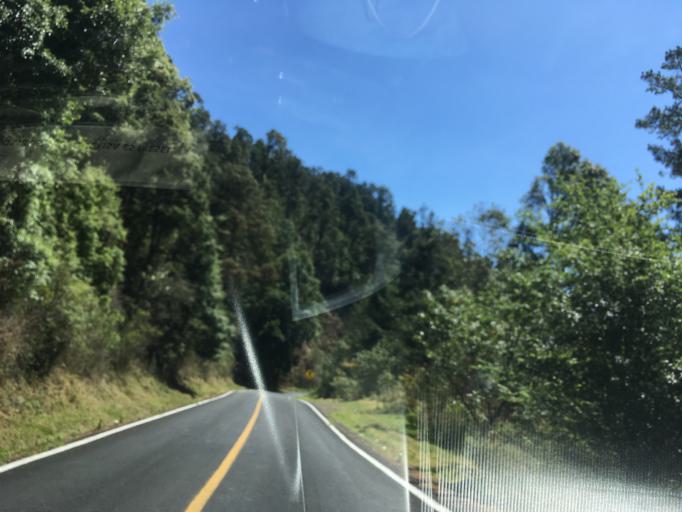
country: MX
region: Michoacan
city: Tzitzio
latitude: 19.6844
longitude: -100.8369
